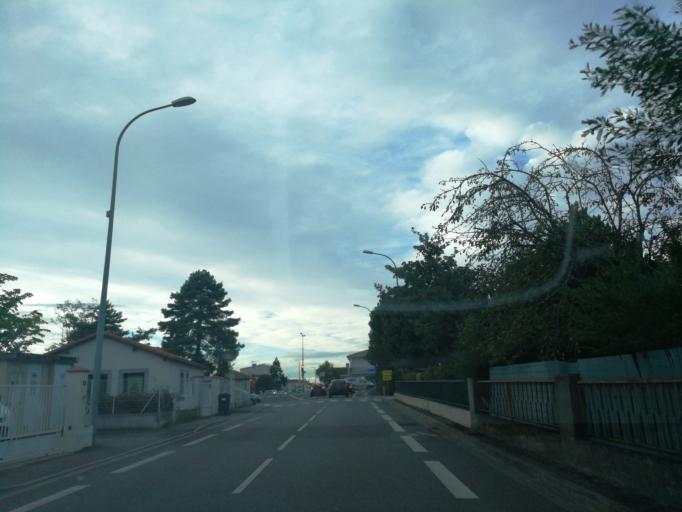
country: FR
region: Midi-Pyrenees
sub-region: Departement de la Haute-Garonne
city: L'Union
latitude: 43.6562
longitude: 1.4805
